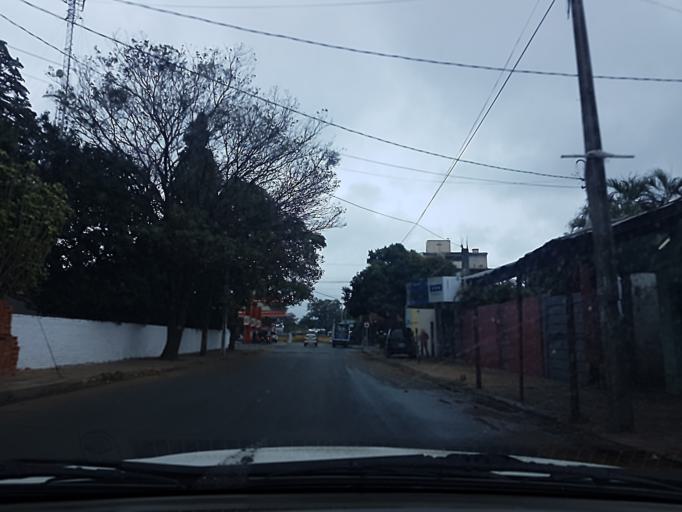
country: PY
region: Central
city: San Lorenzo
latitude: -25.2683
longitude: -57.4839
